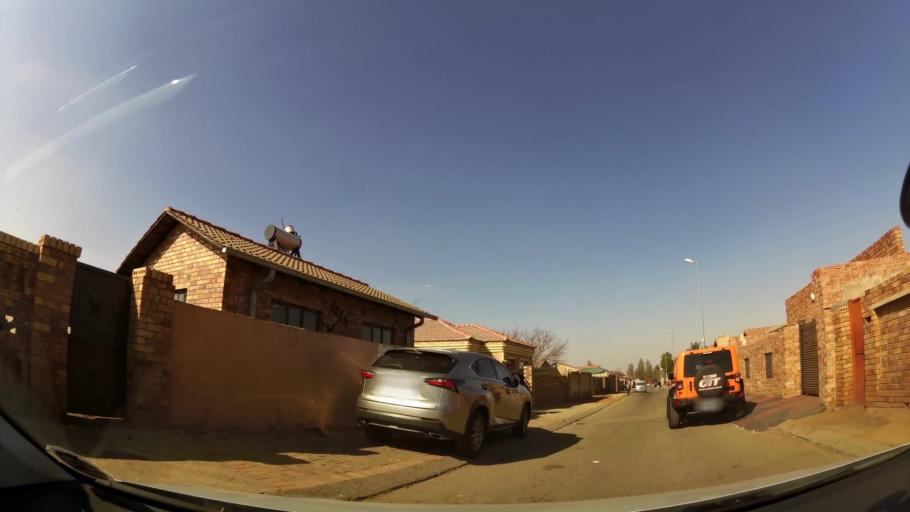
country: ZA
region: Gauteng
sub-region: City of Johannesburg Metropolitan Municipality
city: Soweto
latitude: -26.2801
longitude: 27.8650
